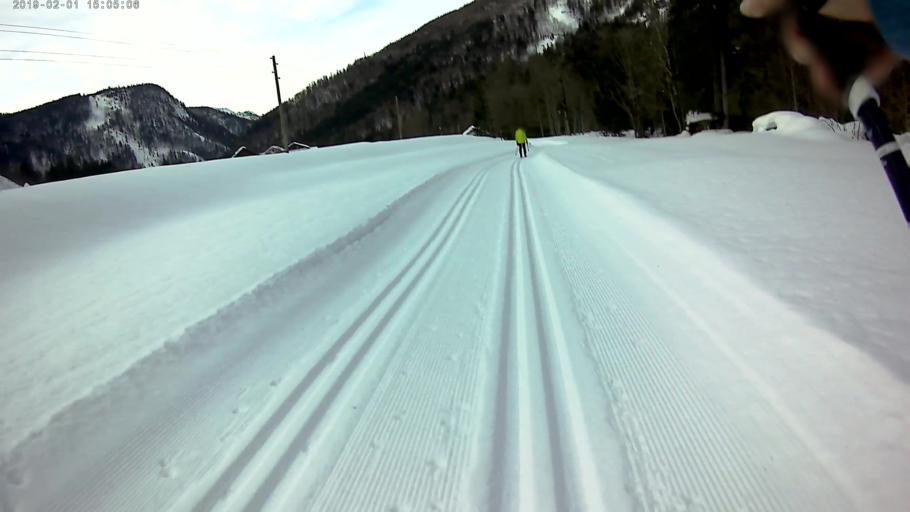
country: AT
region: Salzburg
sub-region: Politischer Bezirk Salzburg-Umgebung
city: Hintersee
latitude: 47.7111
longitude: 13.3056
